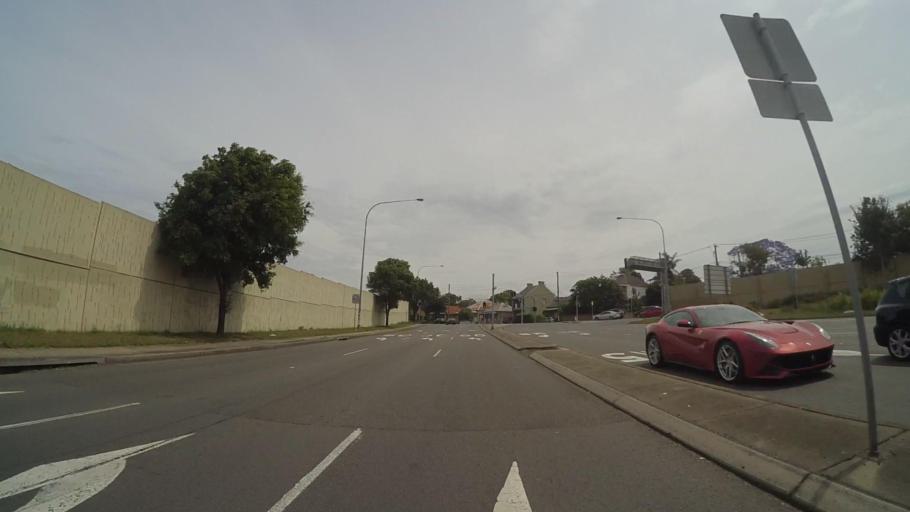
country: AU
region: New South Wales
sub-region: Rockdale
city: Arncliffe
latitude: -33.9381
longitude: 151.1524
